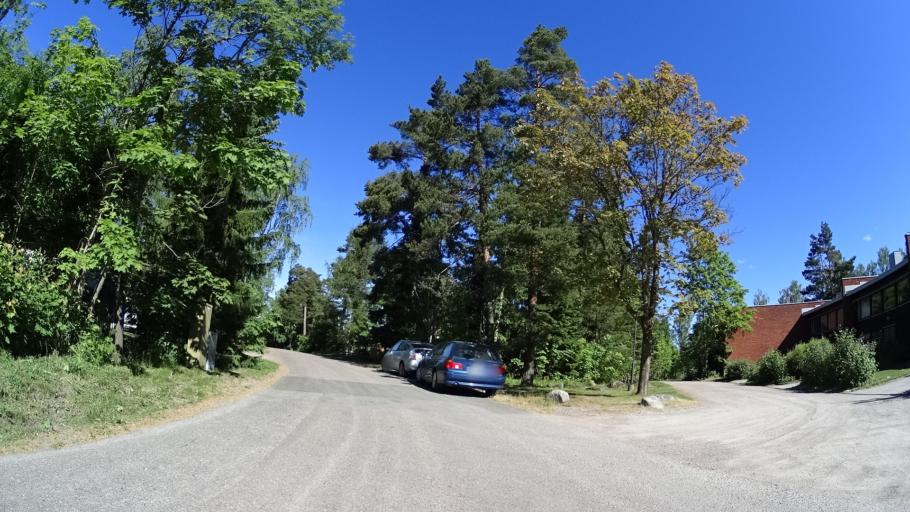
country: FI
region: Uusimaa
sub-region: Helsinki
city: Kauniainen
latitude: 60.2058
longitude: 24.7255
